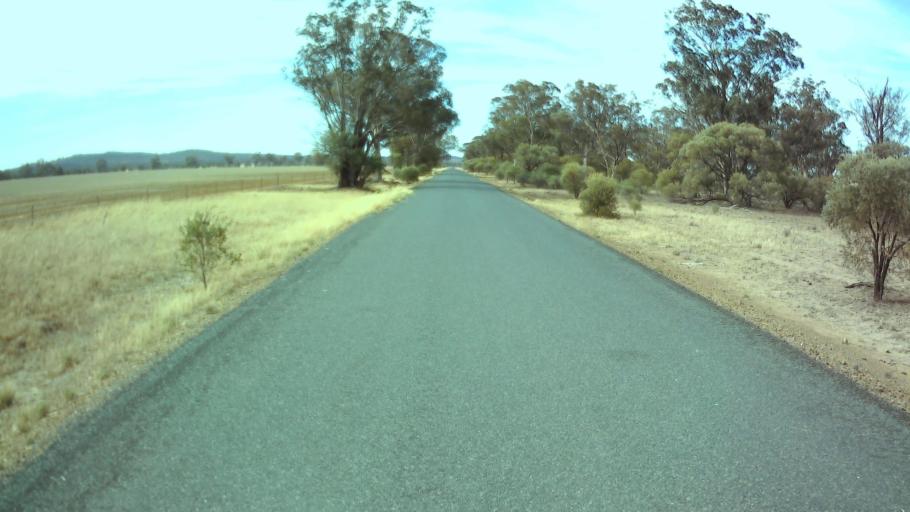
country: AU
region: New South Wales
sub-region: Weddin
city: Grenfell
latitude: -33.8650
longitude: 147.8591
